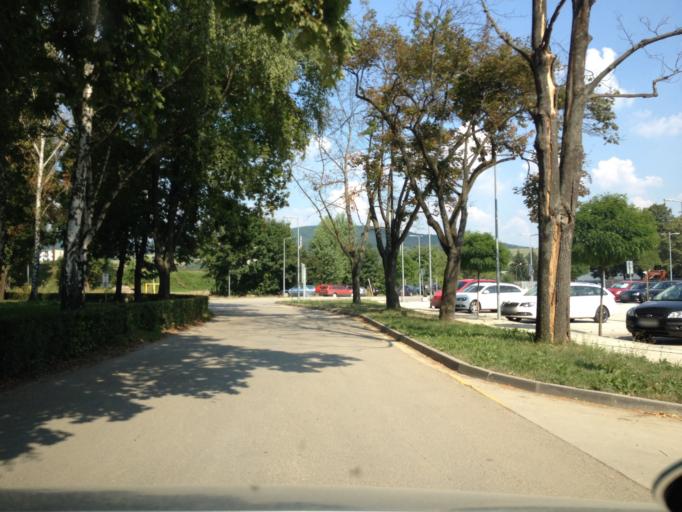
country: SK
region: Nitriansky
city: Puchov
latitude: 49.1061
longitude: 18.3178
